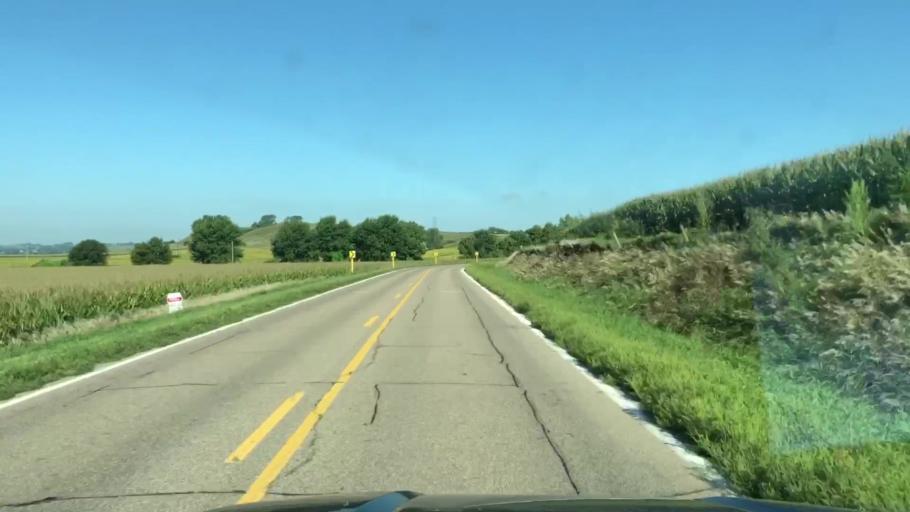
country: US
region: Iowa
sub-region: Woodbury County
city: Sergeant Bluff
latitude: 42.4082
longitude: -96.2546
